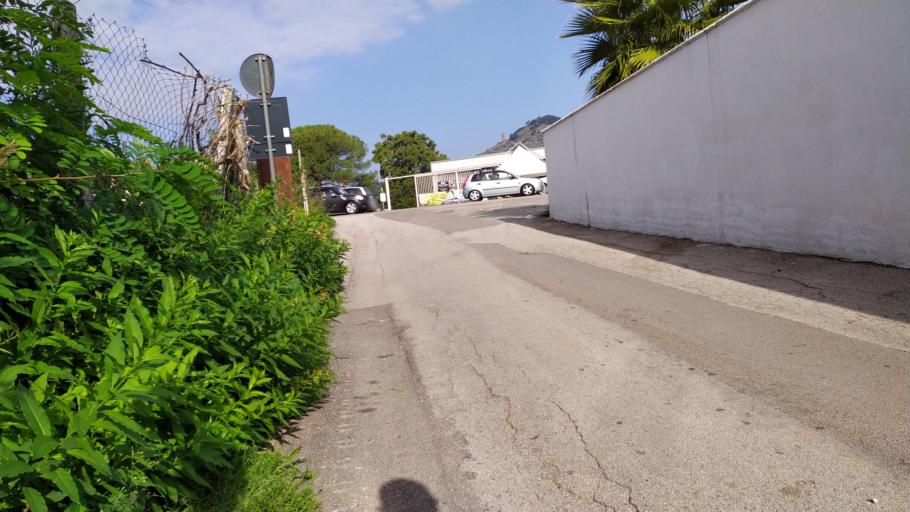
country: IT
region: Campania
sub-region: Provincia di Caserta
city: Maddaloni
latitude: 41.0292
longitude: 14.3961
